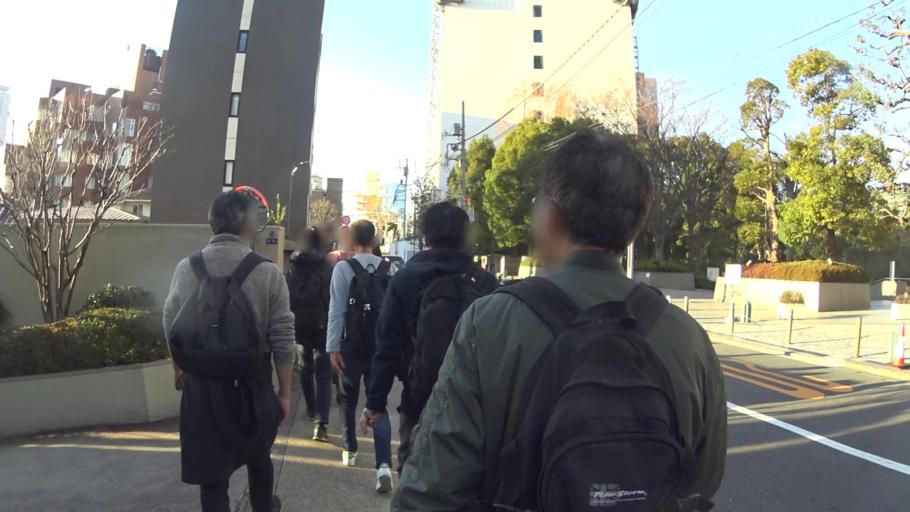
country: JP
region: Tokyo
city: Tokyo
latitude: 35.6720
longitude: 139.7331
